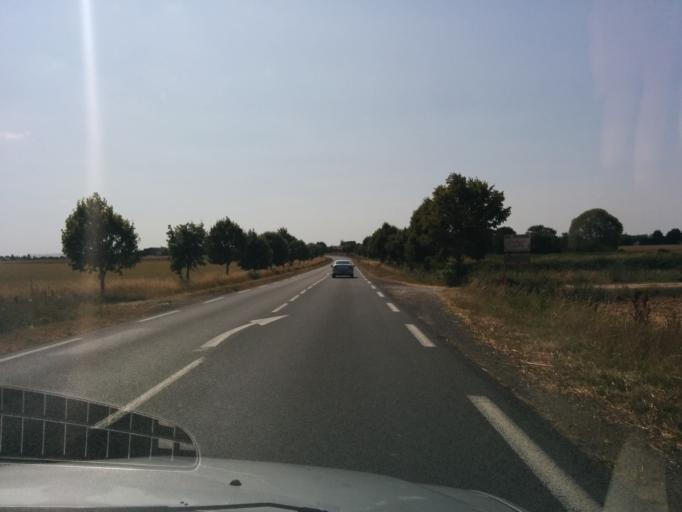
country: FR
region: Poitou-Charentes
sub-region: Departement de la Vienne
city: Neuville-de-Poitou
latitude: 46.6875
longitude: 0.2837
